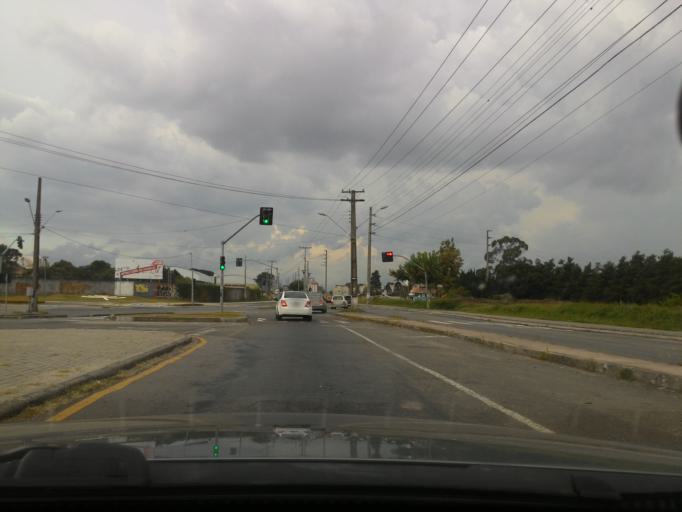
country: BR
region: Parana
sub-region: Pinhais
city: Pinhais
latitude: -25.4438
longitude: -49.1966
